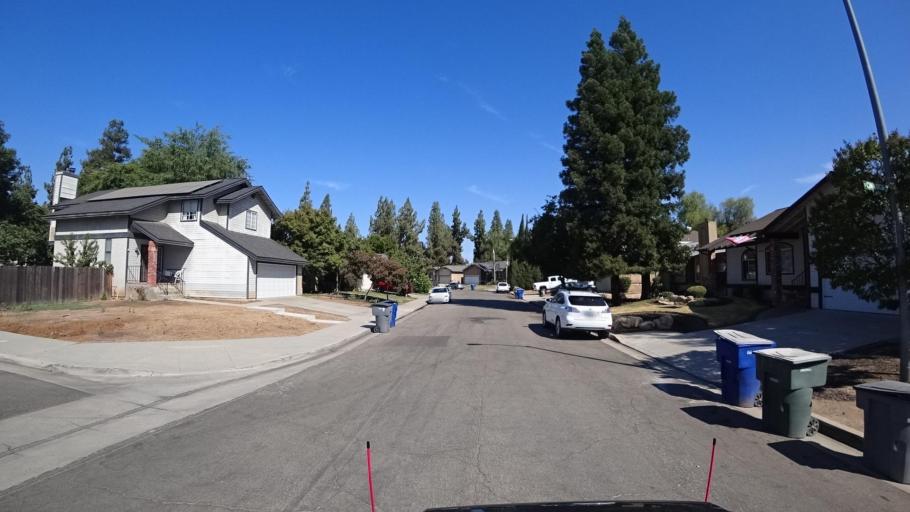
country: US
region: California
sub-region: Fresno County
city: Sunnyside
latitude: 36.7455
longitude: -119.6809
